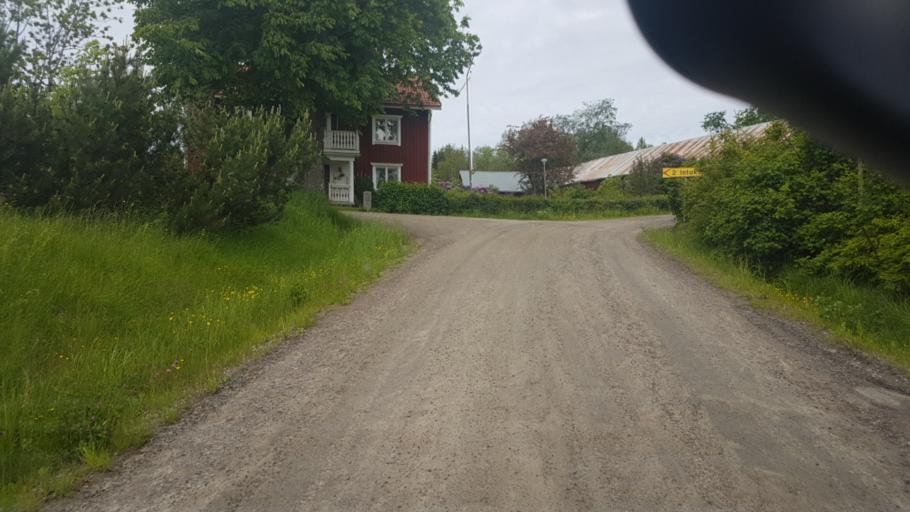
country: SE
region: Vaermland
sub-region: Arvika Kommun
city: Arvika
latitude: 59.8266
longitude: 12.5444
